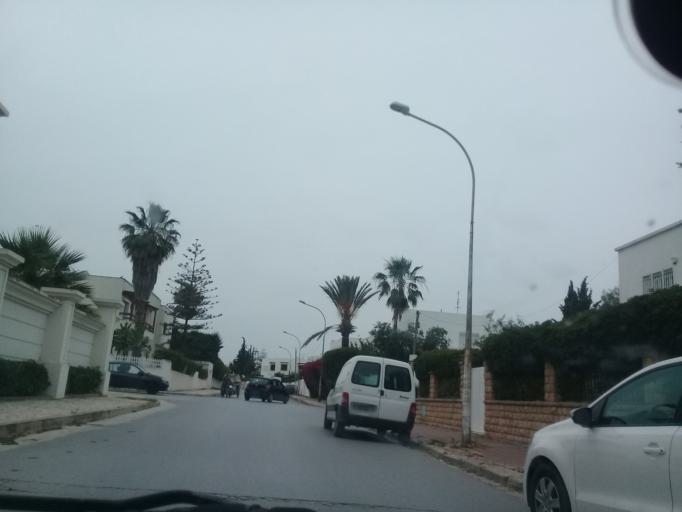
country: TN
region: Tunis
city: Tunis
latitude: 36.8449
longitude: 10.1604
